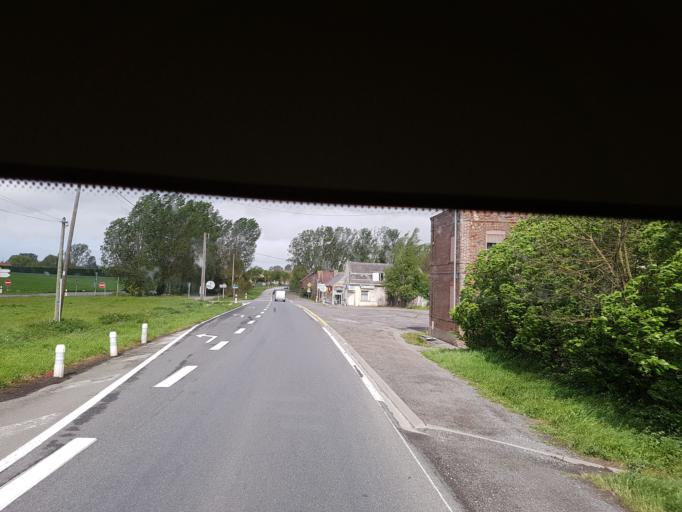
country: FR
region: Nord-Pas-de-Calais
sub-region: Departement du Nord
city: Raillencourt-Sainte-Olle
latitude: 50.2096
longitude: 3.1905
